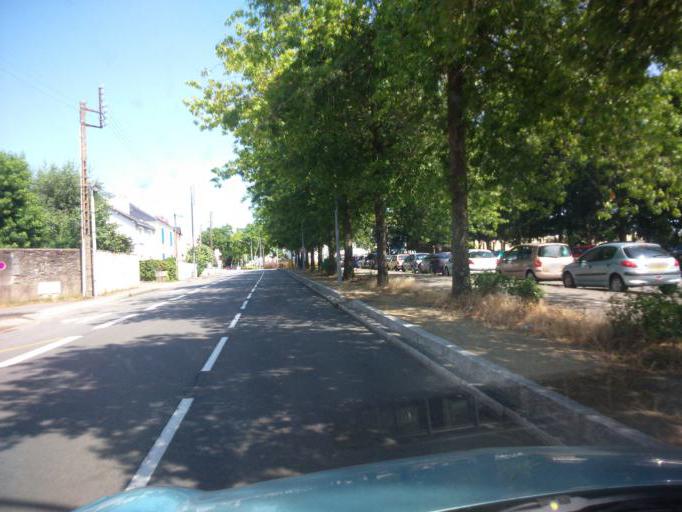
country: FR
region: Pays de la Loire
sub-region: Departement de la Loire-Atlantique
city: Reze
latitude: 47.1997
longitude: -1.5306
